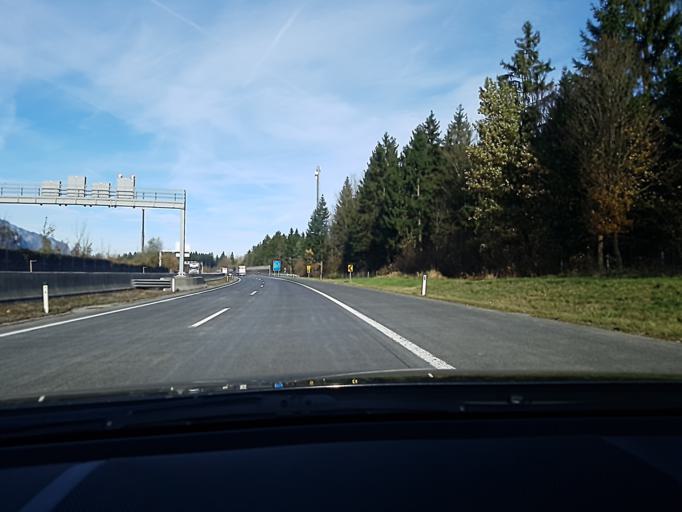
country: AT
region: Salzburg
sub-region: Politischer Bezirk Hallein
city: Adnet
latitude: 47.6549
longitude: 13.1356
